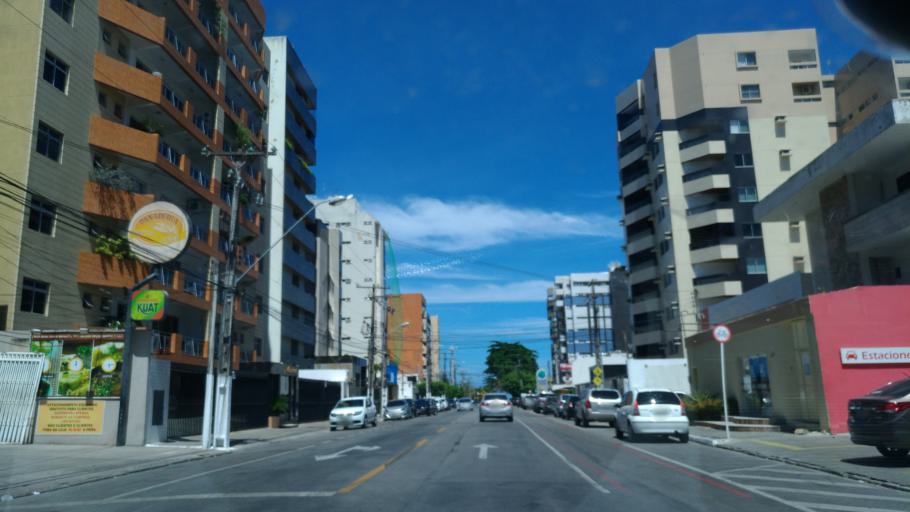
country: BR
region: Alagoas
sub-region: Maceio
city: Maceio
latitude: -9.6567
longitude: -35.7015
